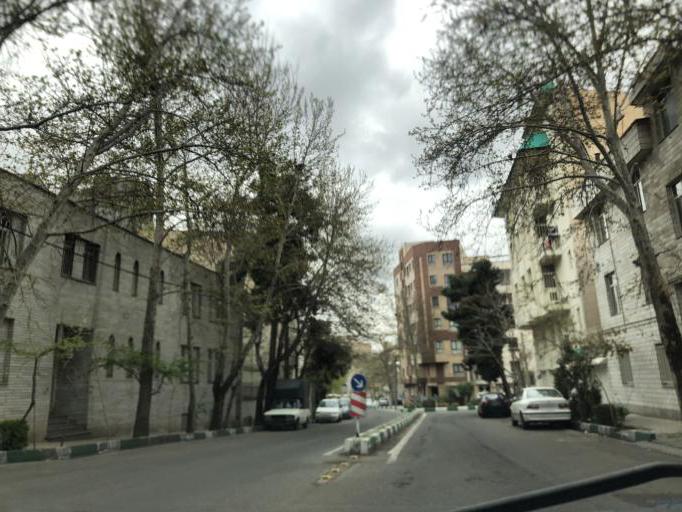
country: IR
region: Tehran
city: Tajrish
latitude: 35.7801
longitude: 51.4653
